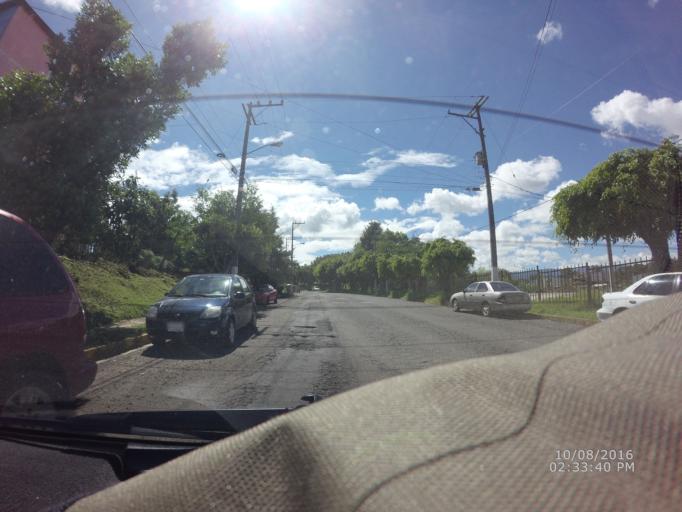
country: MX
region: Veracruz
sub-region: Xalapa
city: Lomas Verdes
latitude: 19.5131
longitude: -96.9018
